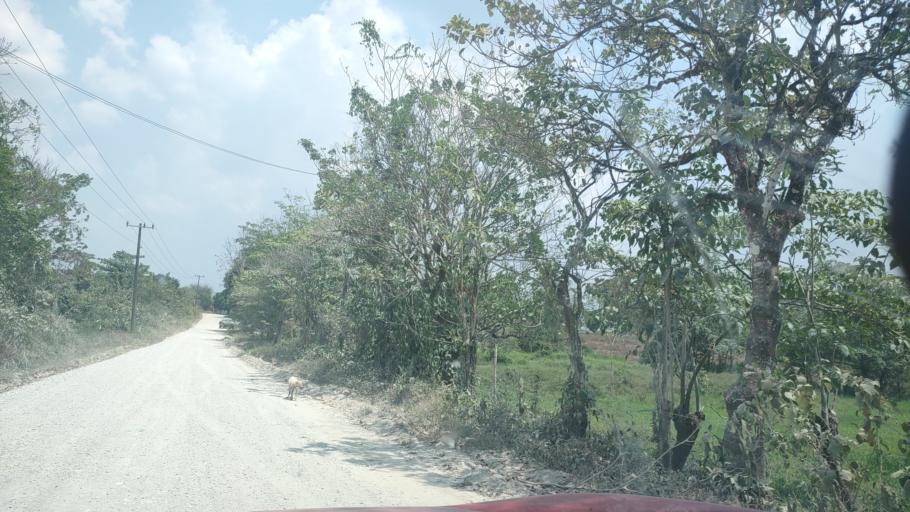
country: MX
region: Tabasco
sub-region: Huimanguillo
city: Francisco Rueda
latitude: 17.6130
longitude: -93.9156
